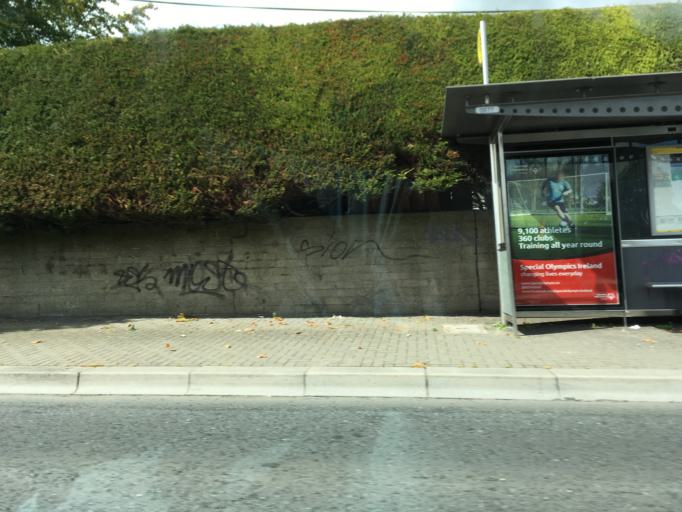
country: IE
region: Leinster
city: Little Bray
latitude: 53.1881
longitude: -6.1274
